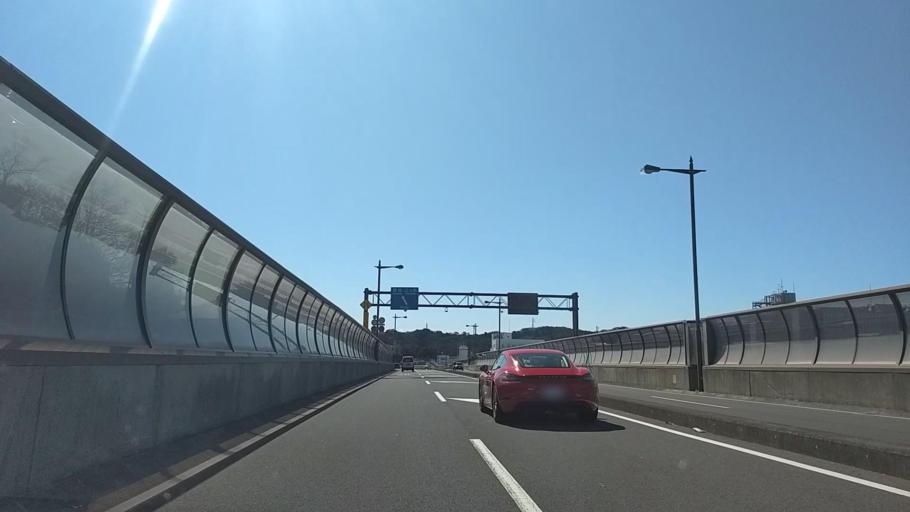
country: JP
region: Kanagawa
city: Fujisawa
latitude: 35.3376
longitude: 139.5023
